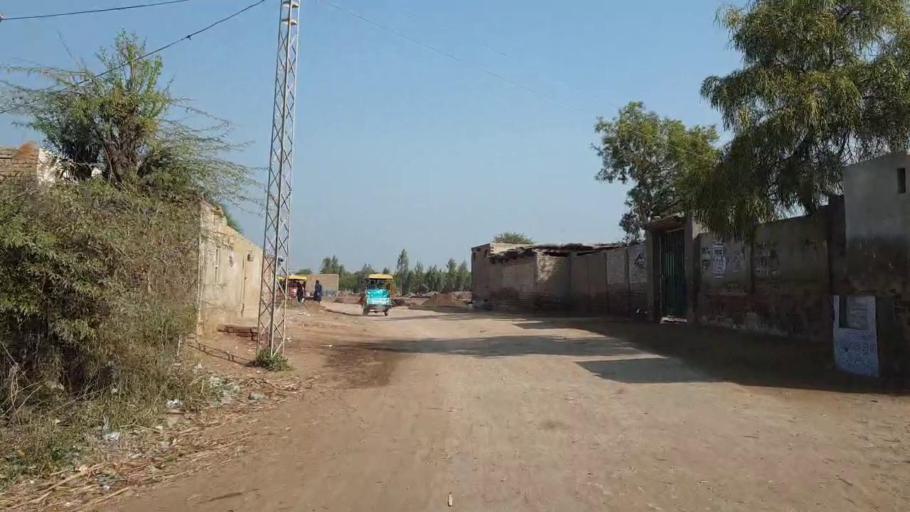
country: PK
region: Sindh
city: Tando Adam
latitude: 25.6761
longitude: 68.5661
